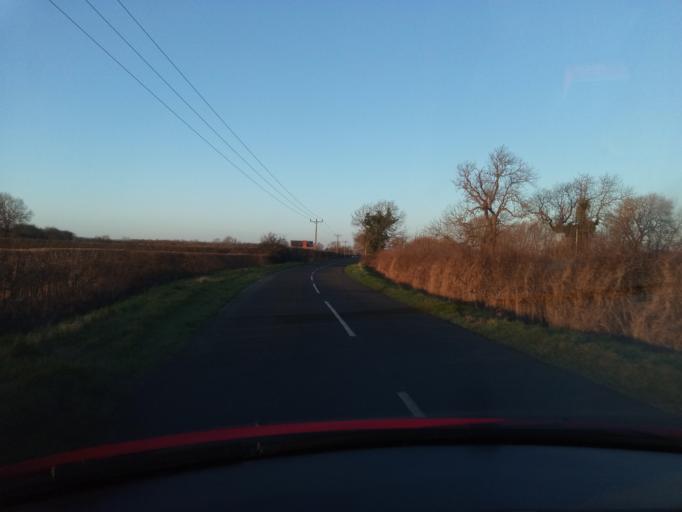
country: GB
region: England
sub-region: Leicestershire
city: Barrow upon Soar
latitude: 52.7733
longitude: -1.1425
